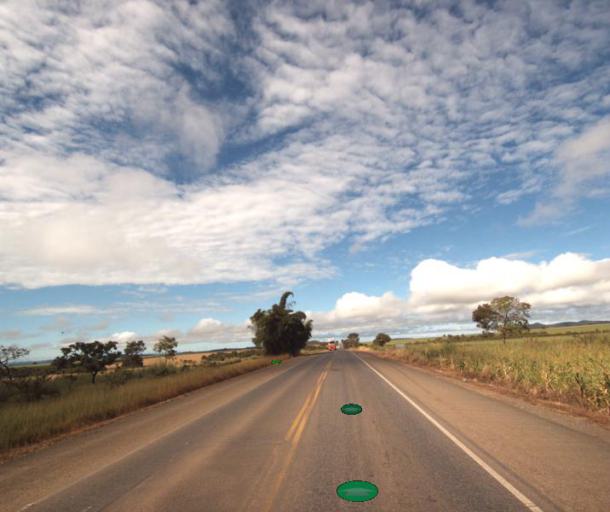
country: BR
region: Goias
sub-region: Uruacu
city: Uruacu
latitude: -14.6966
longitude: -49.2162
